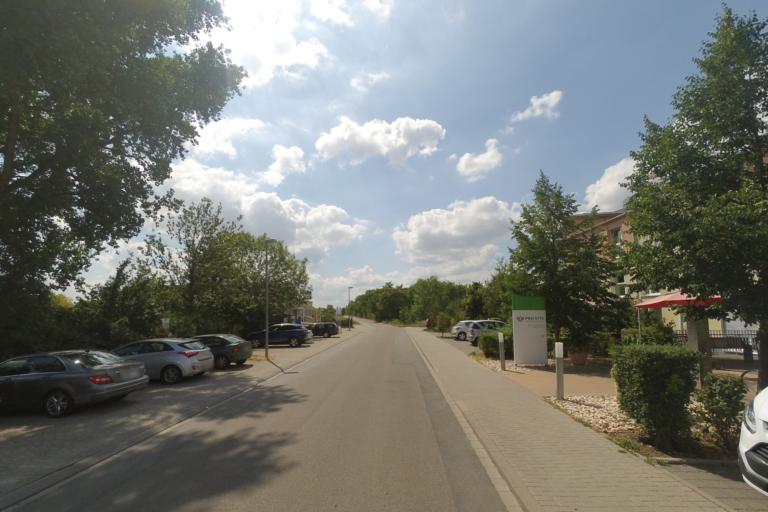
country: DE
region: Rheinland-Pfalz
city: Frankenthal
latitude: 49.5185
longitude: 8.3931
